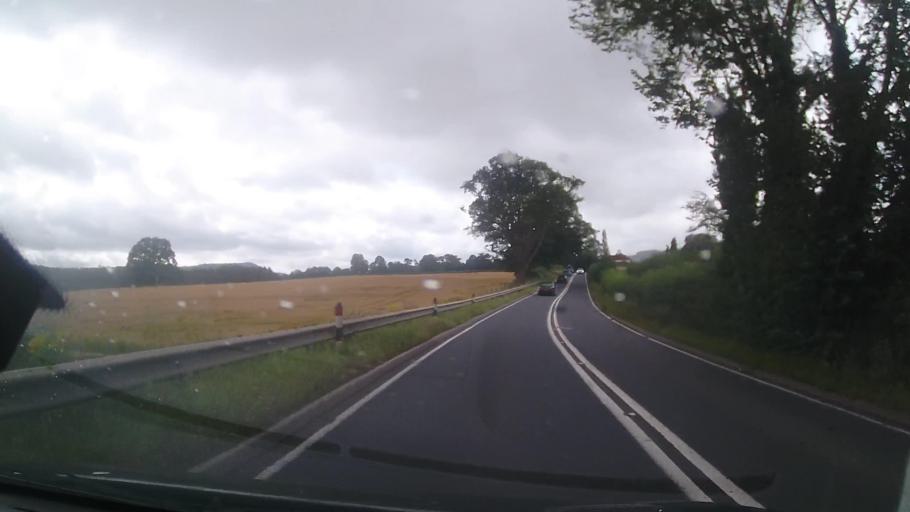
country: GB
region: England
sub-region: Shropshire
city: Craven Arms
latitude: 52.4638
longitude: -2.8280
